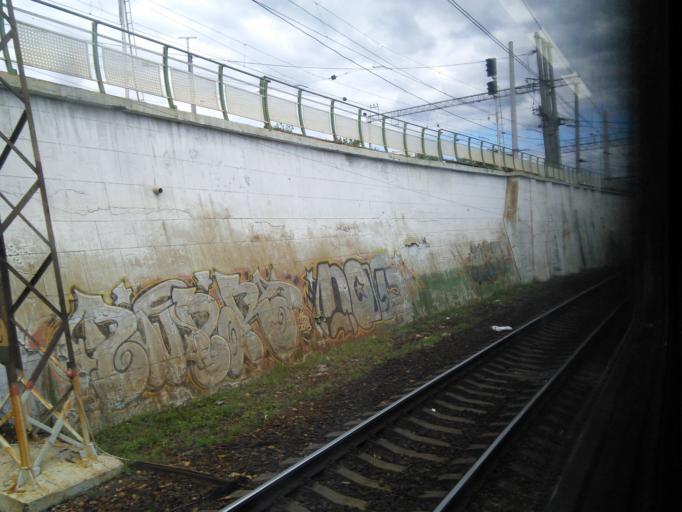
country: RU
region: Moscow
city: Lefortovo
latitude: 55.7819
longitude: 37.6867
